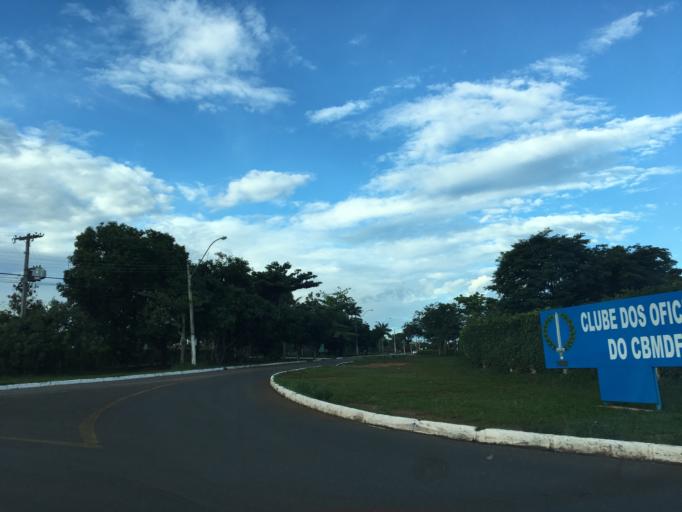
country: BR
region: Federal District
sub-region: Brasilia
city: Brasilia
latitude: -15.8170
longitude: -47.8415
